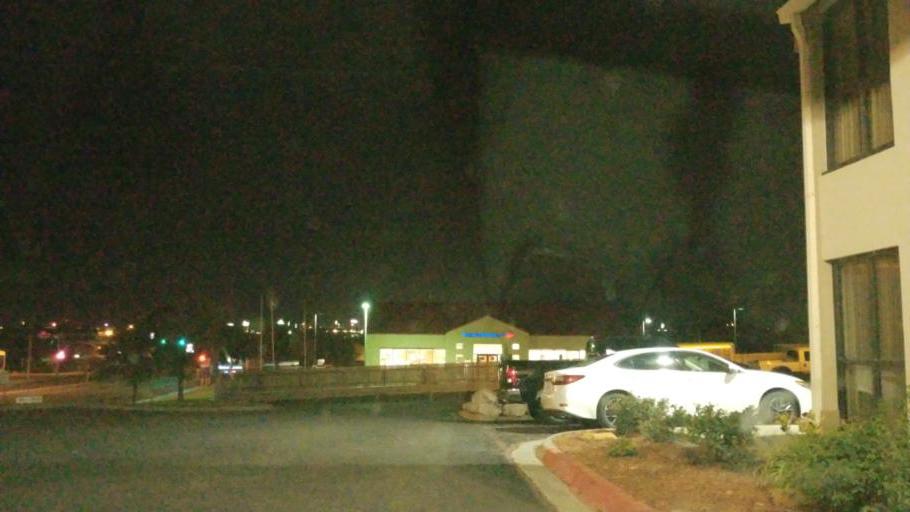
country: US
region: Texas
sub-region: Potter County
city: Amarillo
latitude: 35.1957
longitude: -101.9222
